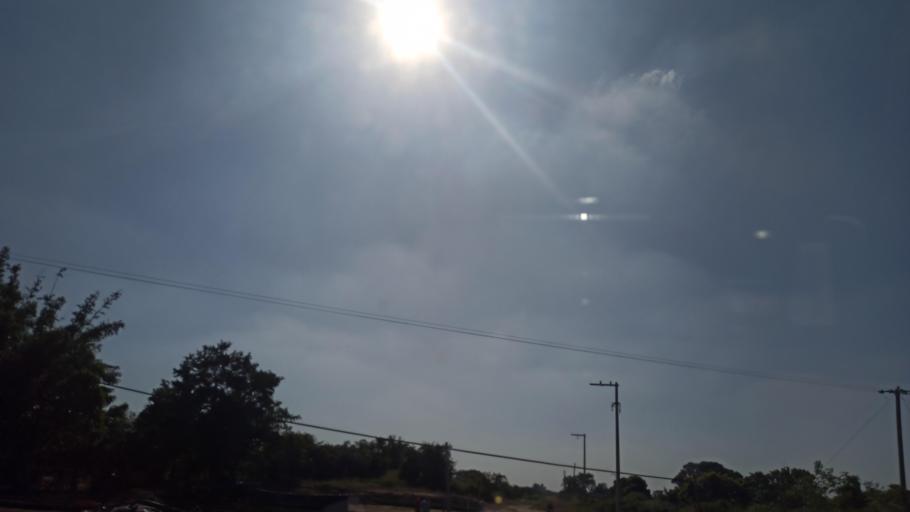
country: MX
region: Veracruz
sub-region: Martinez de la Torre
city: La Union Paso Largo
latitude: 20.1447
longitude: -96.9994
